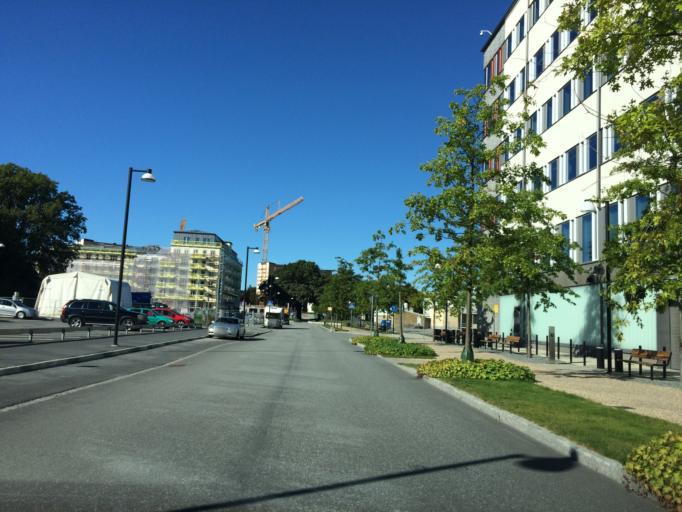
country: SE
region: Stockholm
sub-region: Solna Kommun
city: Solna
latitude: 59.3518
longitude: 18.0107
